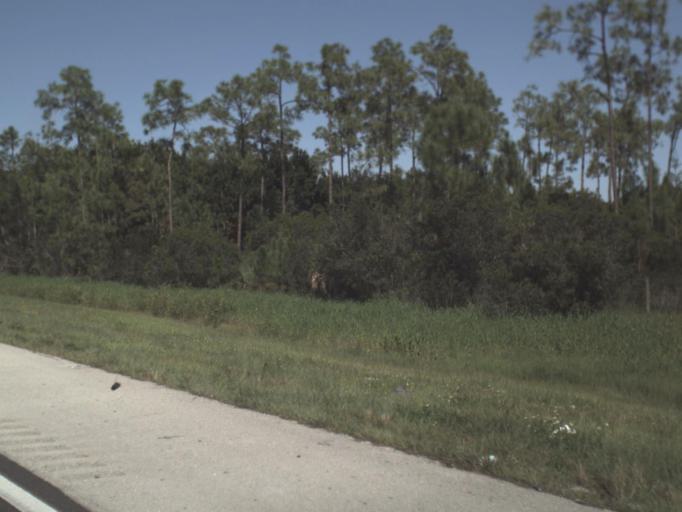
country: US
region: Florida
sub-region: Lee County
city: Three Oaks
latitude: 26.4500
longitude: -81.7841
